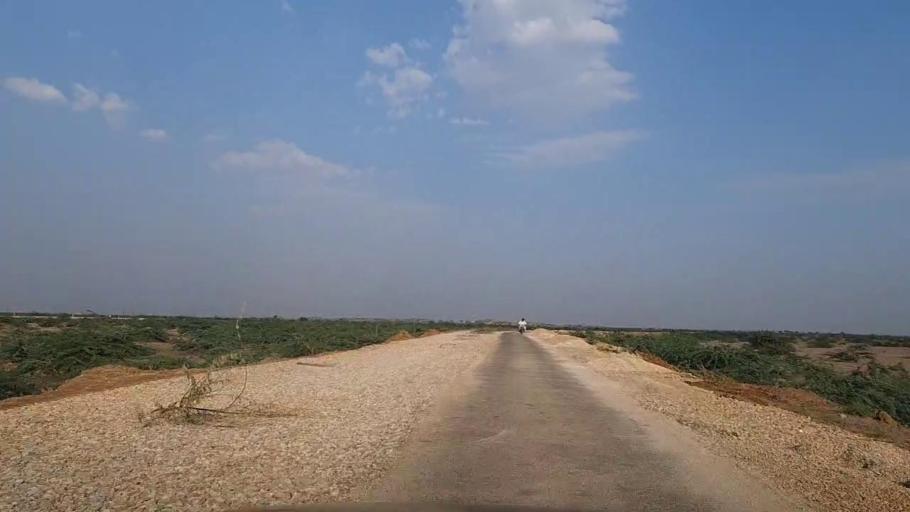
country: PK
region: Sindh
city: Gharo
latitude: 24.8464
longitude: 67.7475
